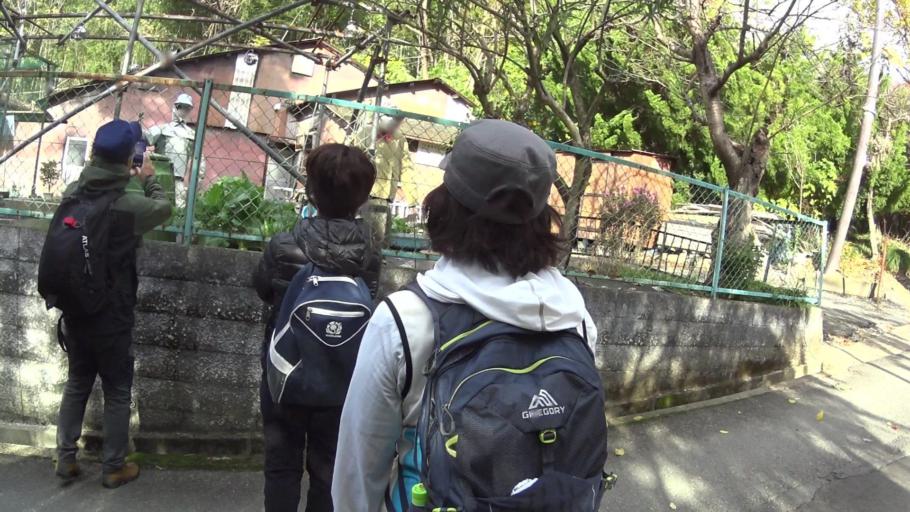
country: JP
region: Kyoto
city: Kyoto
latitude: 34.9630
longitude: 135.7843
